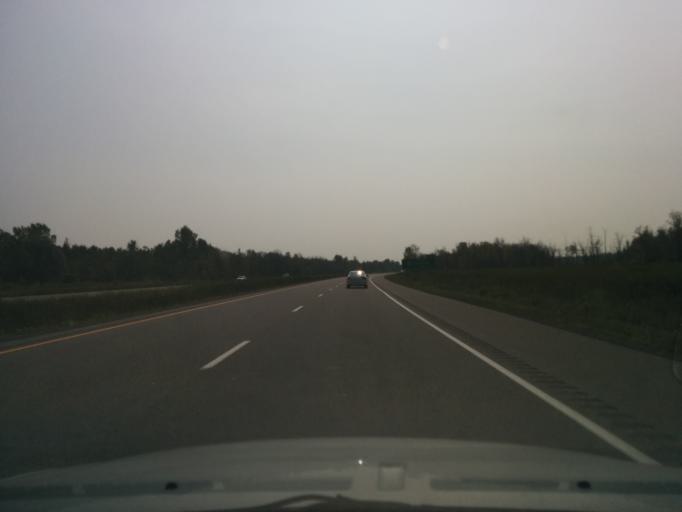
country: CA
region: Ontario
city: Bells Corners
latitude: 45.1054
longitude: -75.6619
